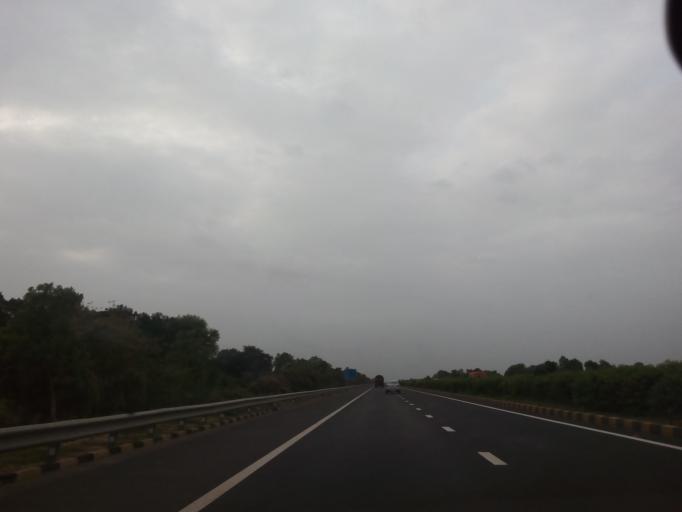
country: IN
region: Gujarat
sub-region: Kheda
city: Chaklasi
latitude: 22.6642
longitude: 72.9193
